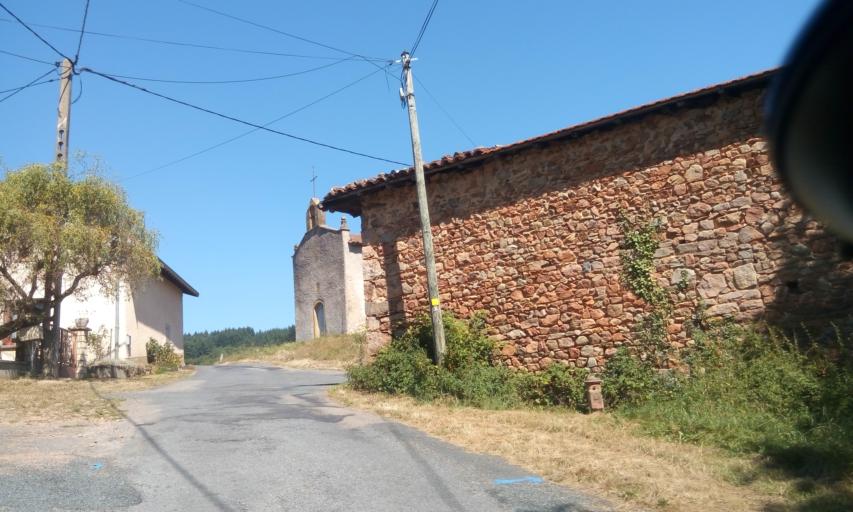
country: FR
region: Rhone-Alpes
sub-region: Departement du Rhone
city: Grandris
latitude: 46.0063
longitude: 4.4531
